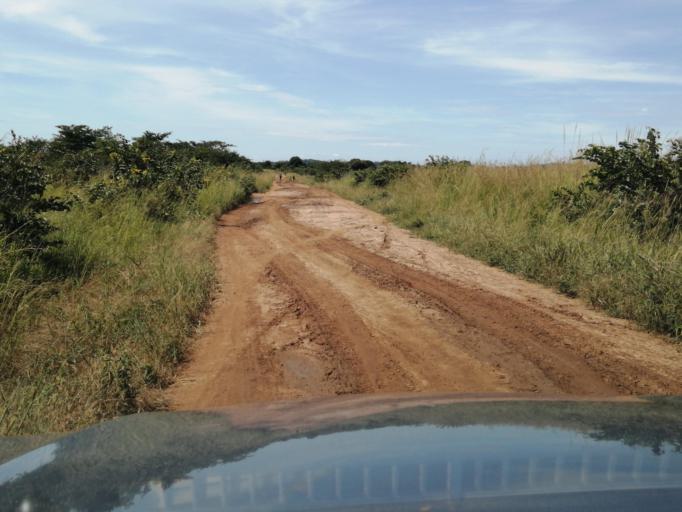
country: ZM
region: Central
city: Chibombo
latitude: -14.9685
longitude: 27.8060
